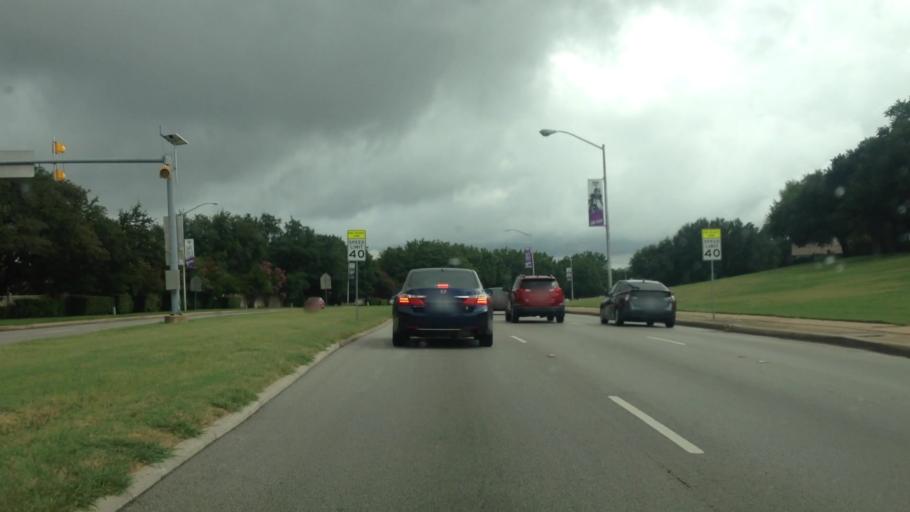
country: US
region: Texas
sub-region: Tarrant County
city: Edgecliff Village
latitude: 32.6884
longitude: -97.3933
